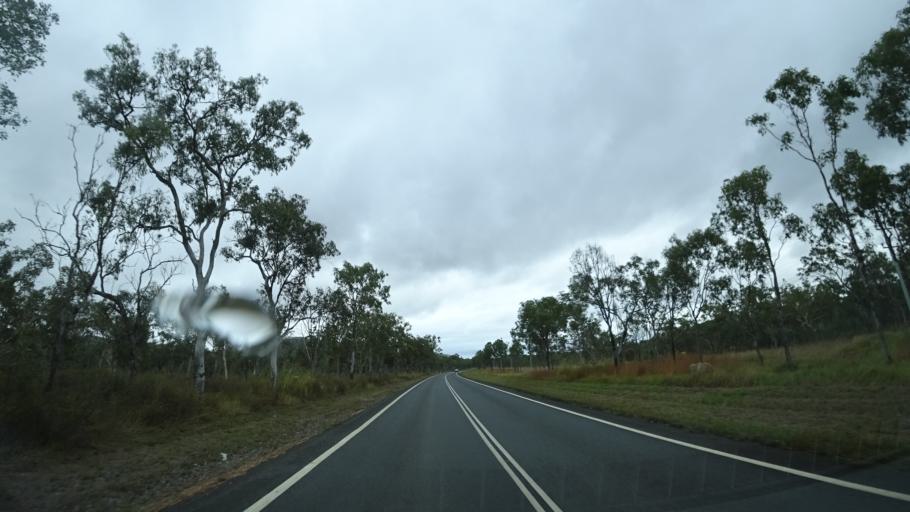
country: AU
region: Queensland
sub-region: Cairns
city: Port Douglas
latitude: -16.7206
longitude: 145.3531
